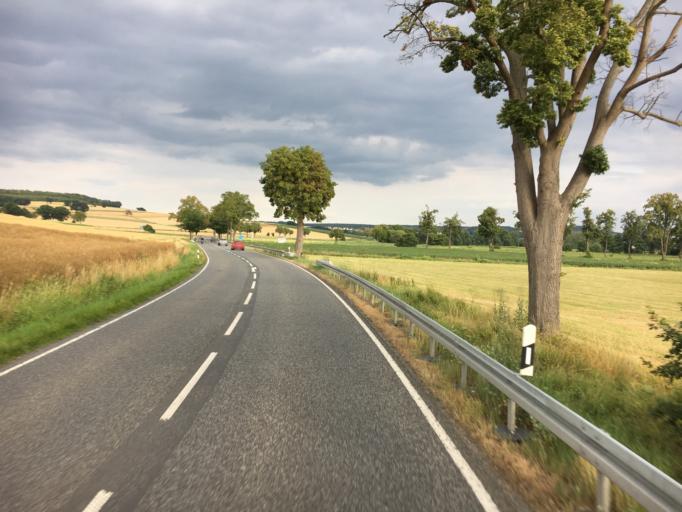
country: DE
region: Hesse
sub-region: Regierungsbezirk Kassel
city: Schrecksbach
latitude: 50.8704
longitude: 9.2722
